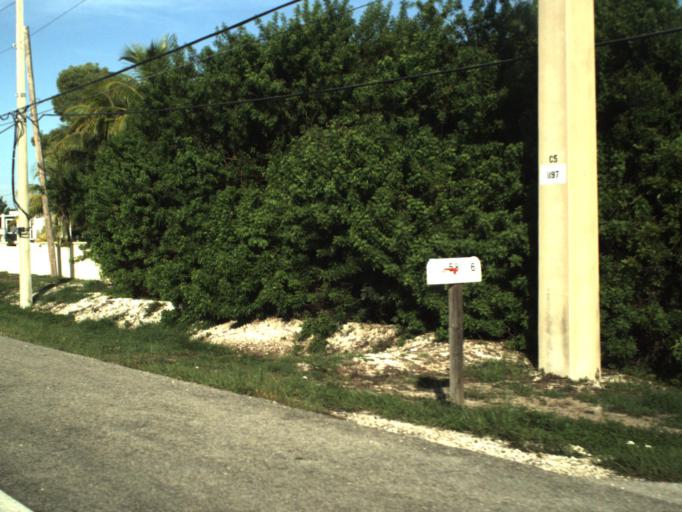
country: US
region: Florida
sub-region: Monroe County
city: Marathon
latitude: 24.7662
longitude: -80.9458
